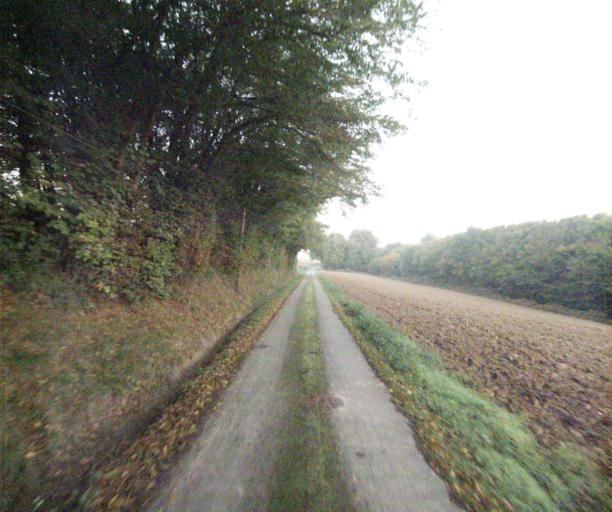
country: FR
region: Midi-Pyrenees
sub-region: Departement du Gers
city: Vic-Fezensac
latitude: 43.7786
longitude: 0.2257
